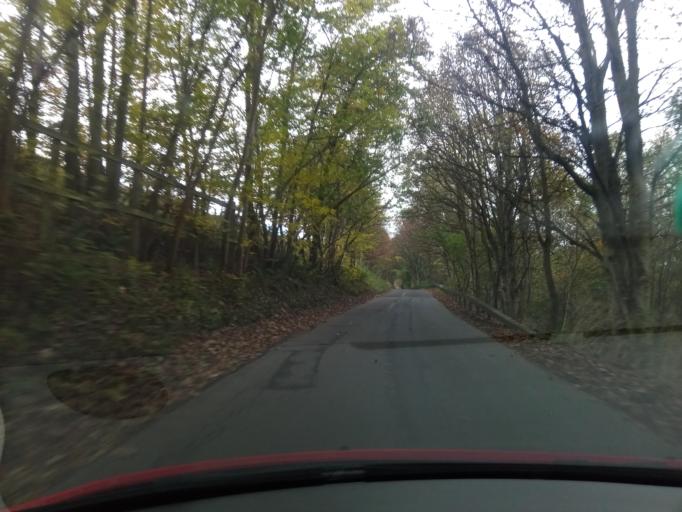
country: GB
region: Scotland
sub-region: The Scottish Borders
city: Peebles
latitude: 55.6325
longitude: -3.1316
